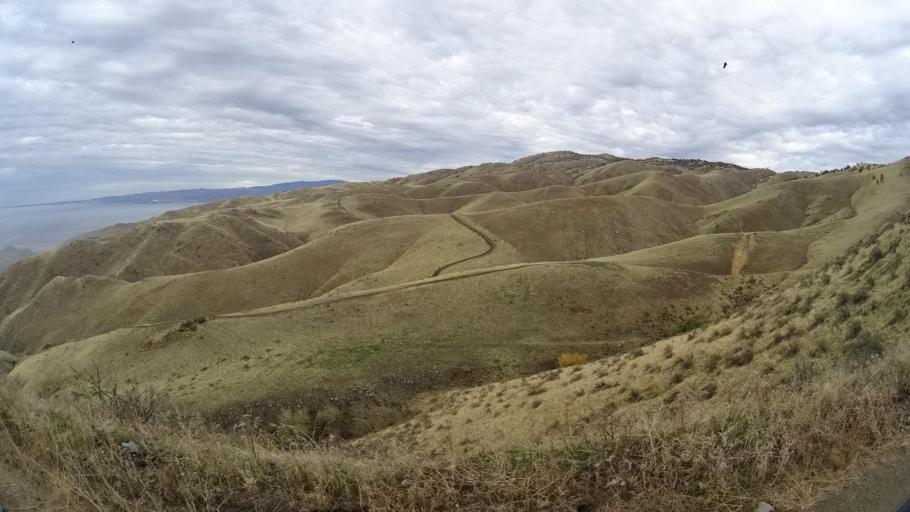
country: US
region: California
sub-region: Kern County
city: Arvin
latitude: 35.1354
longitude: -118.7740
